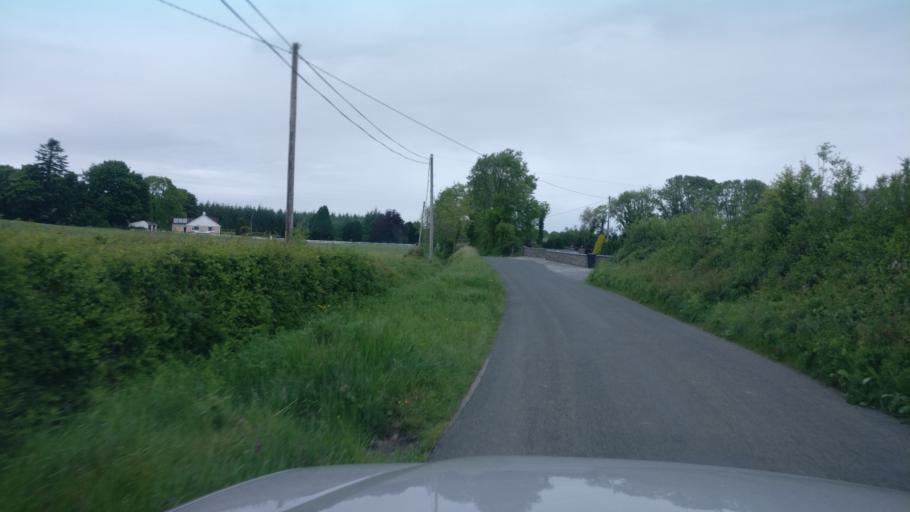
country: IE
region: Connaught
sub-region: County Galway
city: Loughrea
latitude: 53.1150
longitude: -8.4226
